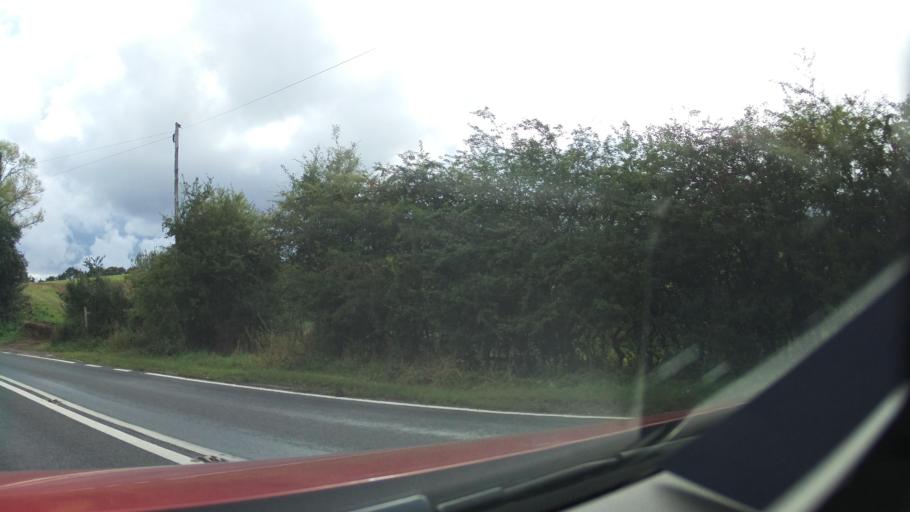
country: GB
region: England
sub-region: Shropshire
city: Bridgnorth
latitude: 52.5636
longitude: -2.3939
